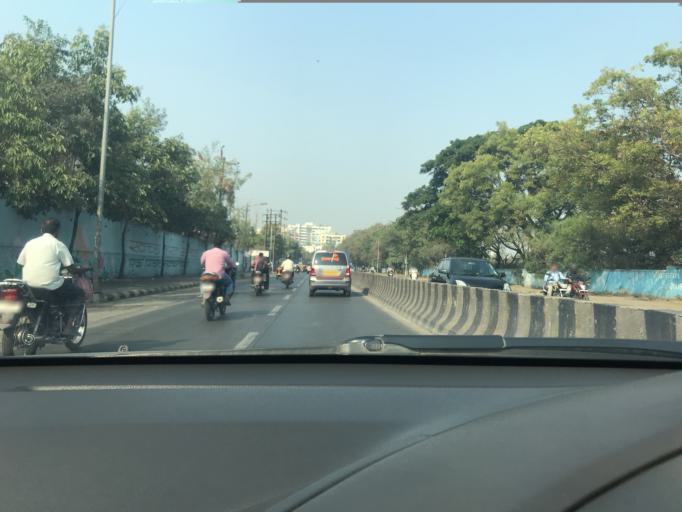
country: IN
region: Maharashtra
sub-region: Pune Division
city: Khadki
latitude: 18.5502
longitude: 73.8084
